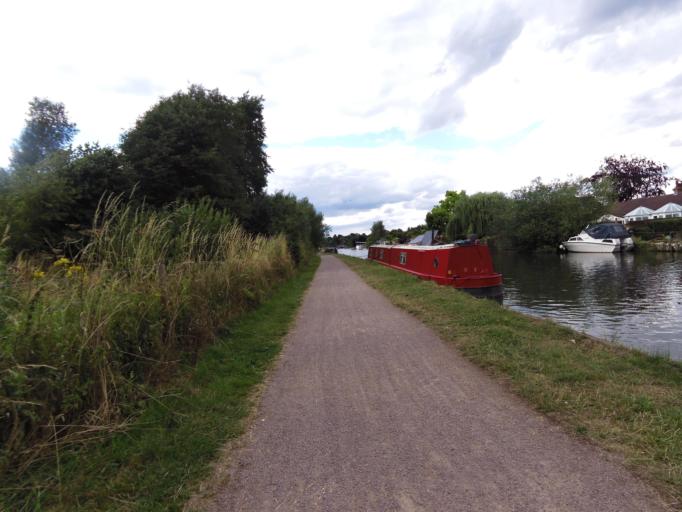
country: GB
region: England
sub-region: Hertfordshire
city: Broxbourne
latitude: 51.7384
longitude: -0.0131
